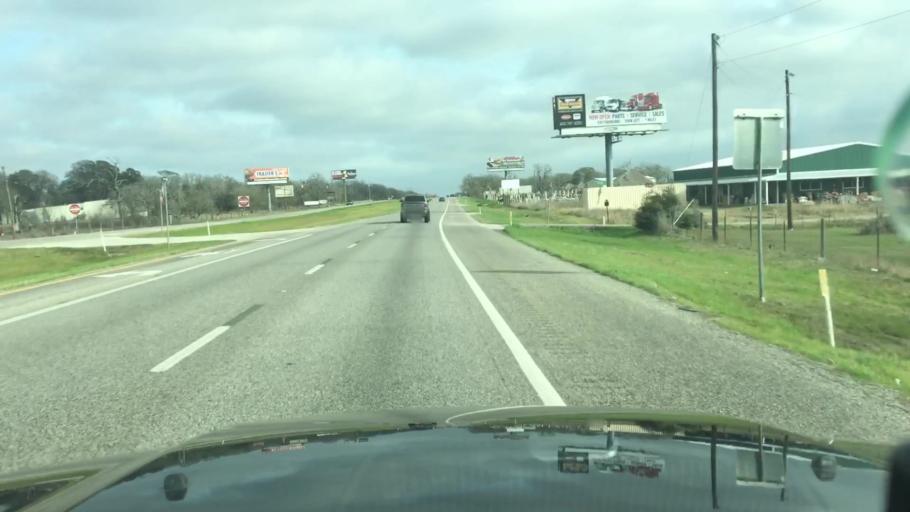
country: US
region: Texas
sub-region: Waller County
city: Hempstead
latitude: 30.1309
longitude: -96.1384
